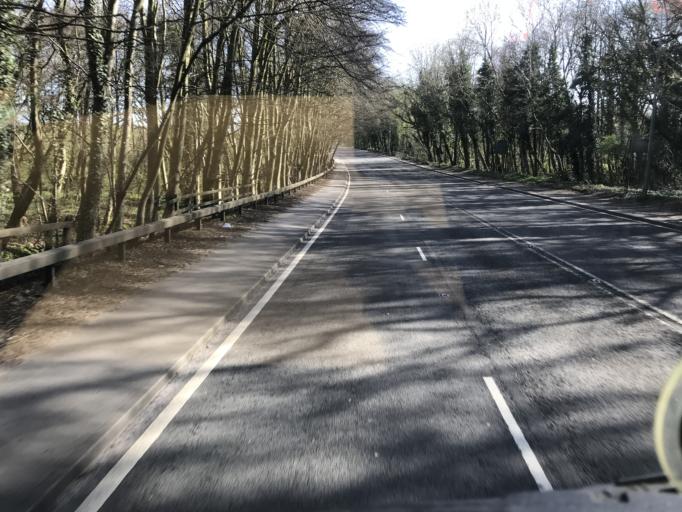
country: GB
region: England
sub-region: Cheshire West and Chester
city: Marston
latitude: 53.2763
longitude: -2.4458
